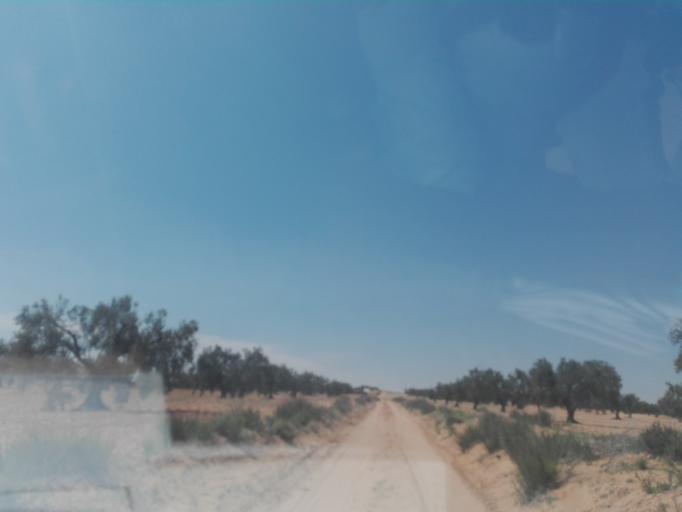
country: TN
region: Safaqis
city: Bi'r `Ali Bin Khalifah
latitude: 34.6039
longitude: 10.3450
